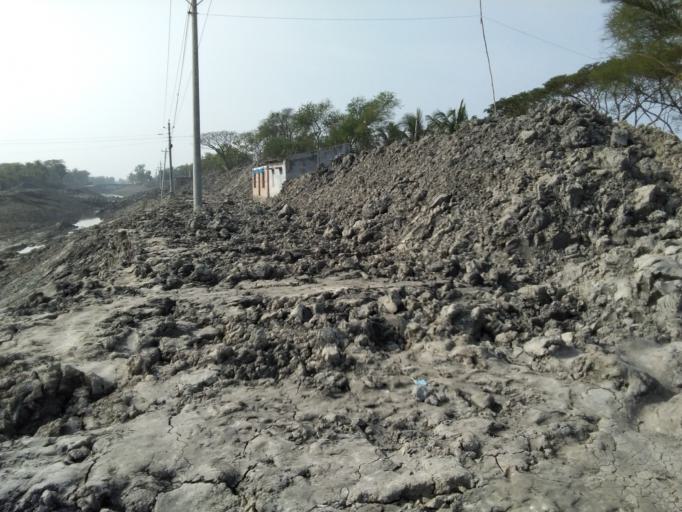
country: IN
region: West Bengal
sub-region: North 24 Parganas
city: Taki
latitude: 22.5920
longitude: 89.0337
